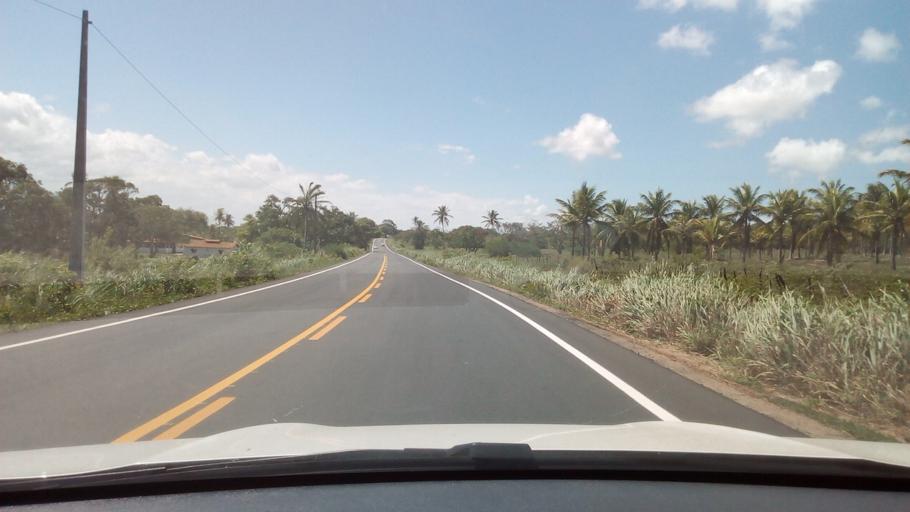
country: BR
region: Rio Grande do Norte
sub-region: Nisia Floresta
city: Nisia Floresta
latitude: -6.0867
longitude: -35.2193
